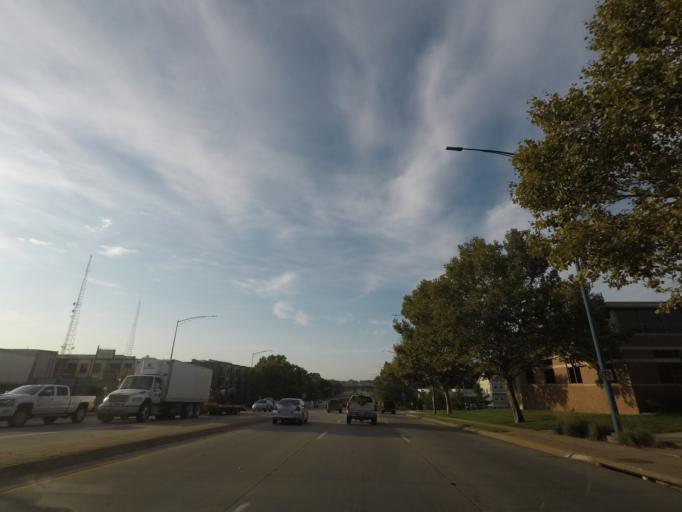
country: US
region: Iowa
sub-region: Polk County
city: Des Moines
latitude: 41.5878
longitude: -93.6449
